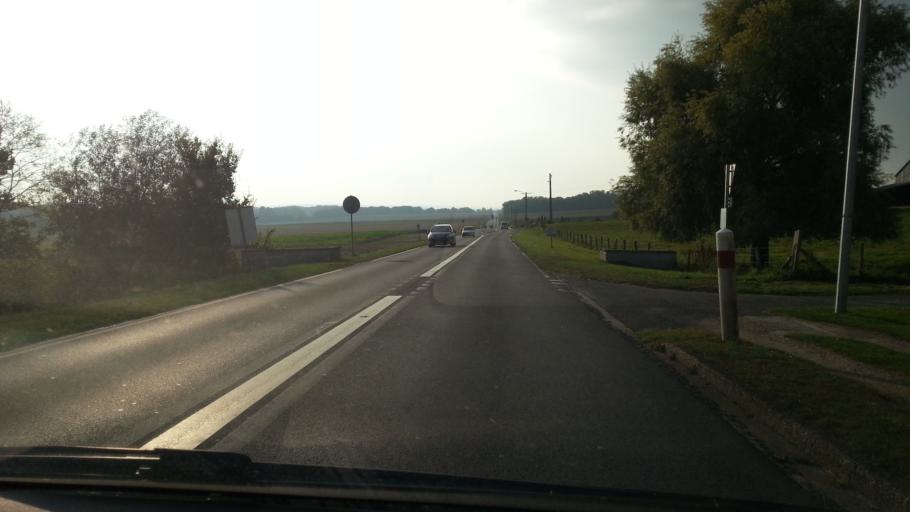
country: FR
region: Picardie
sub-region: Departement de l'Oise
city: Guiscard
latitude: 49.5842
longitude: 3.0846
